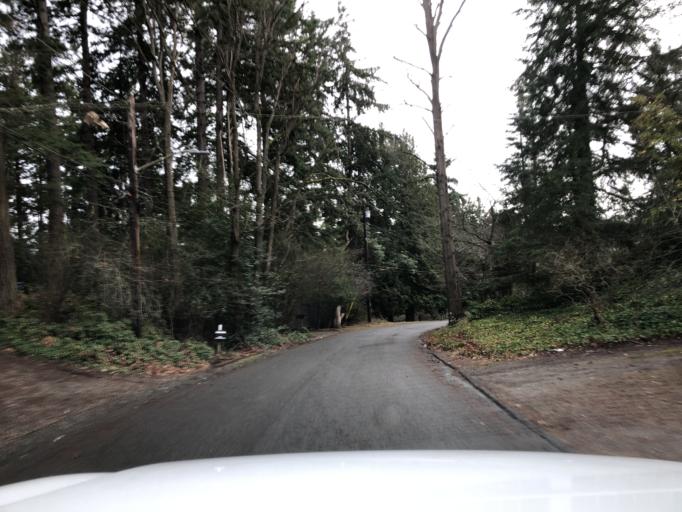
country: US
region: Washington
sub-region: King County
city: Lake Forest Park
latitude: 47.7108
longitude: -122.2981
